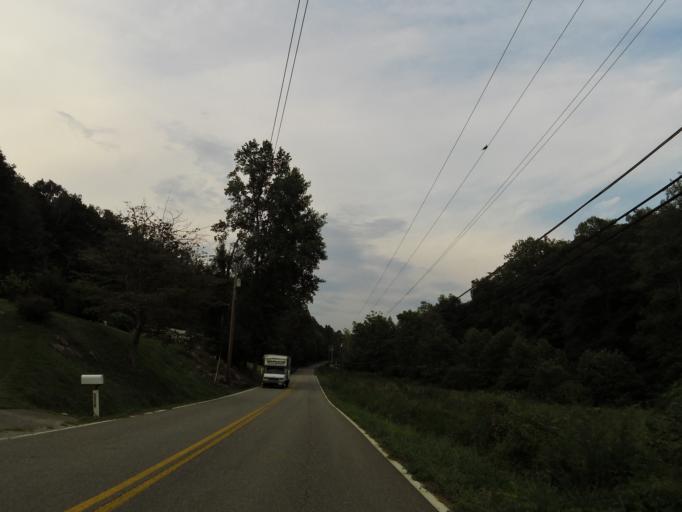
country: US
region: Tennessee
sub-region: Anderson County
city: Clinton
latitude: 36.1276
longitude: -84.2221
